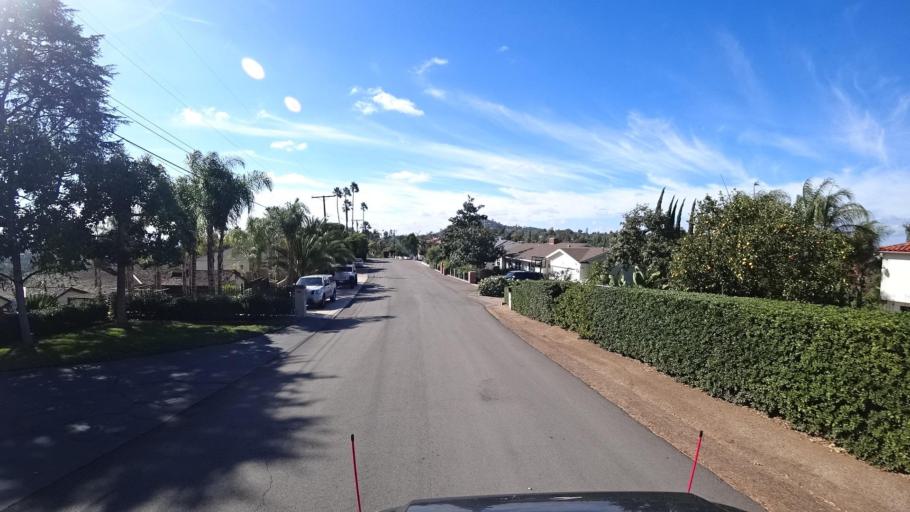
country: US
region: California
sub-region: San Diego County
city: Casa de Oro-Mount Helix
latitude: 32.7612
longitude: -116.9582
